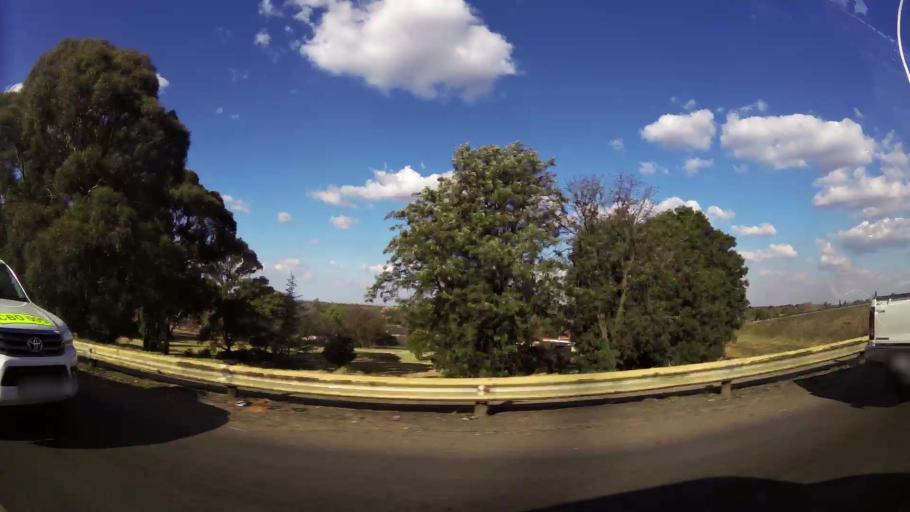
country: ZA
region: Mpumalanga
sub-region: Nkangala District Municipality
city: Witbank
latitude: -25.8886
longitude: 29.2323
